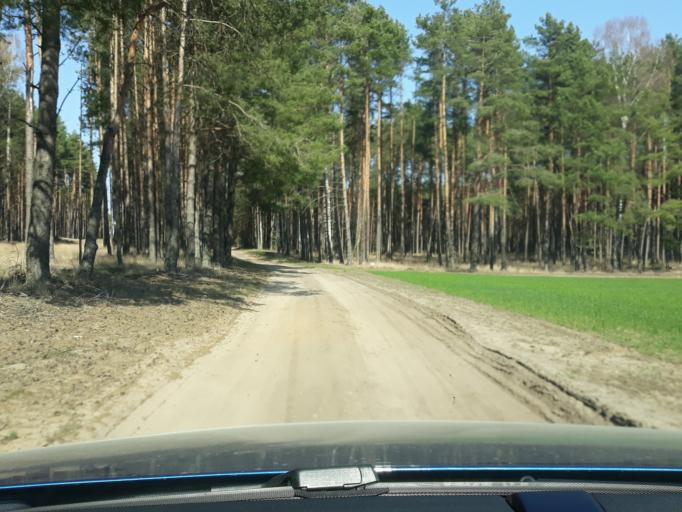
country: PL
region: Pomeranian Voivodeship
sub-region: Powiat bytowski
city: Lipnica
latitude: 53.8676
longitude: 17.4313
